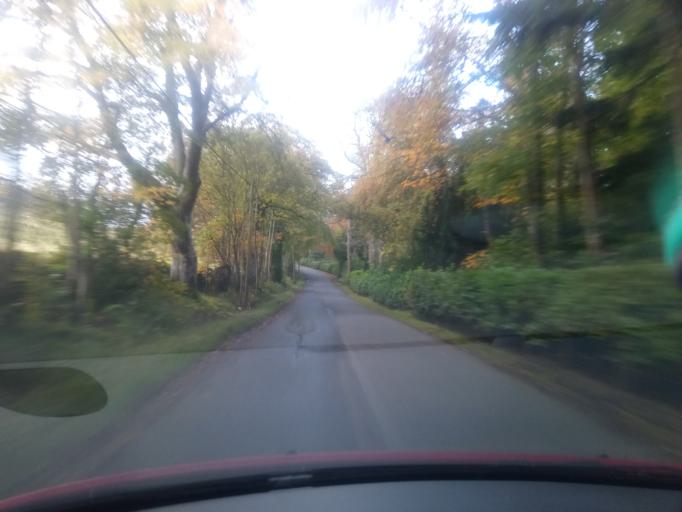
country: GB
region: Scotland
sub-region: The Scottish Borders
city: Jedburgh
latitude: 55.3747
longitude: -2.6471
